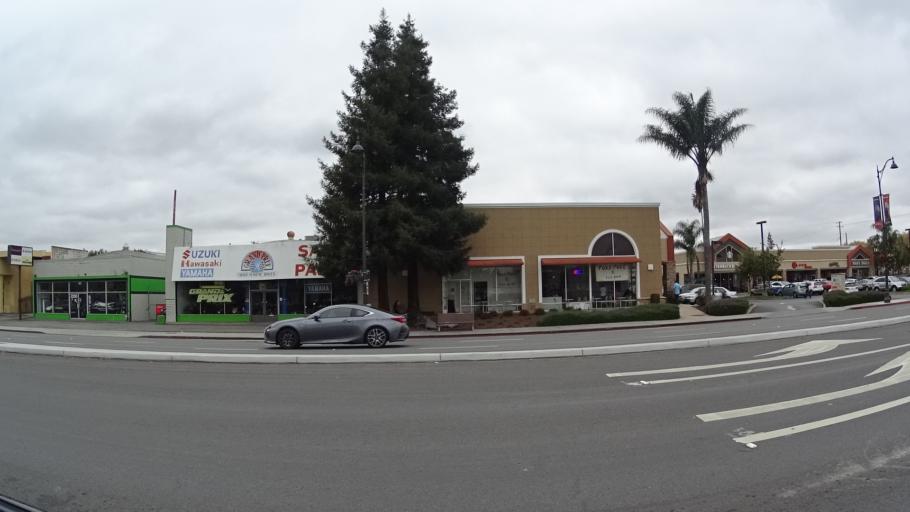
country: US
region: California
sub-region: Santa Clara County
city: Santa Clara
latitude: 37.3524
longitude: -121.9672
